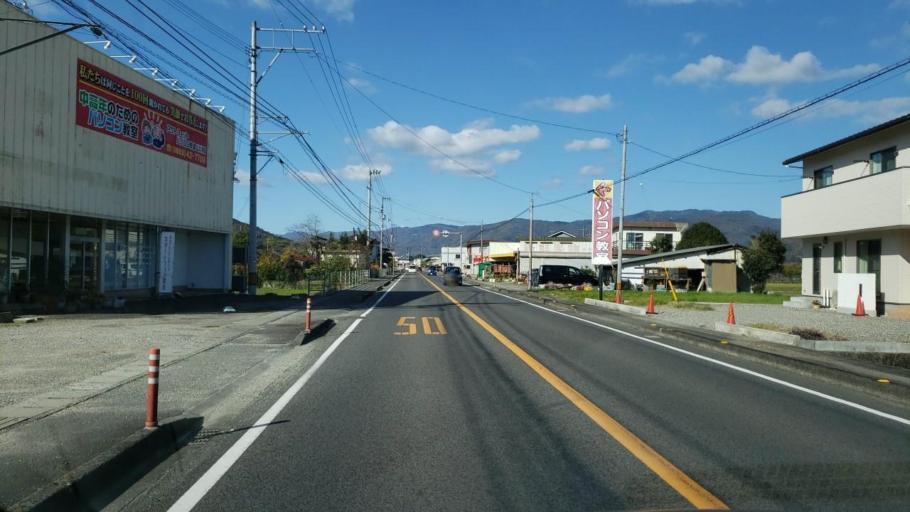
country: JP
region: Tokushima
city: Wakimachi
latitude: 34.0591
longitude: 134.2185
